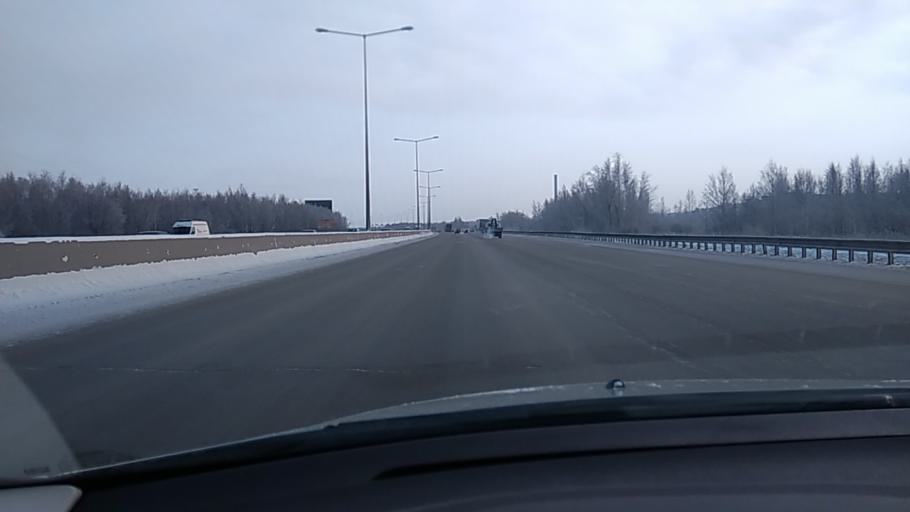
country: RU
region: Sverdlovsk
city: Istok
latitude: 56.7656
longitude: 60.7444
